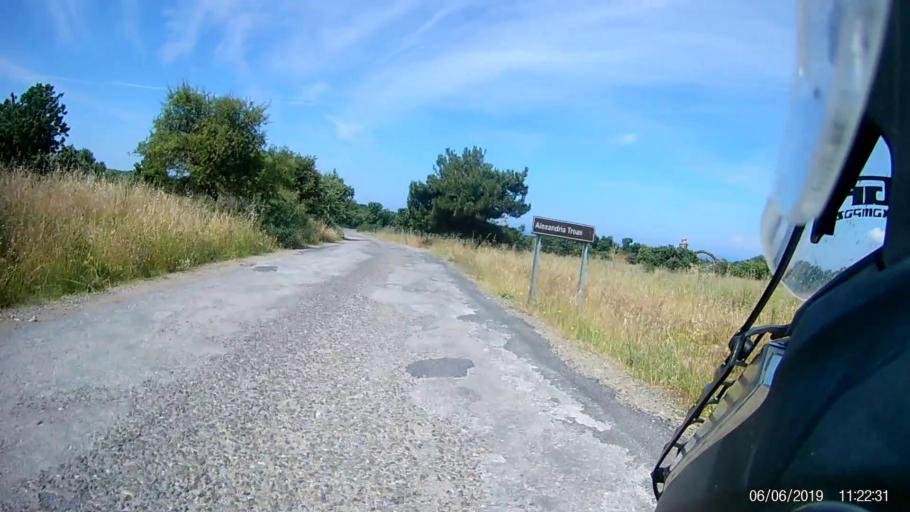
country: TR
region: Canakkale
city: Gulpinar
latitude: 39.6111
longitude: 26.1857
